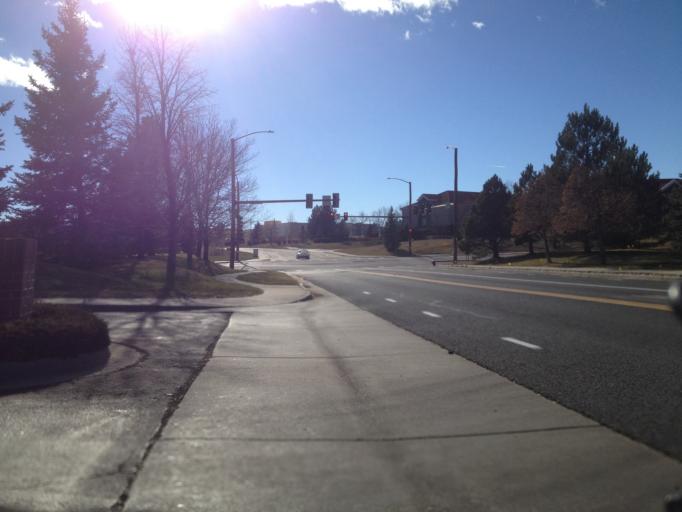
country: US
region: Colorado
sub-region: Boulder County
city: Superior
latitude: 39.9593
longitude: -105.1601
